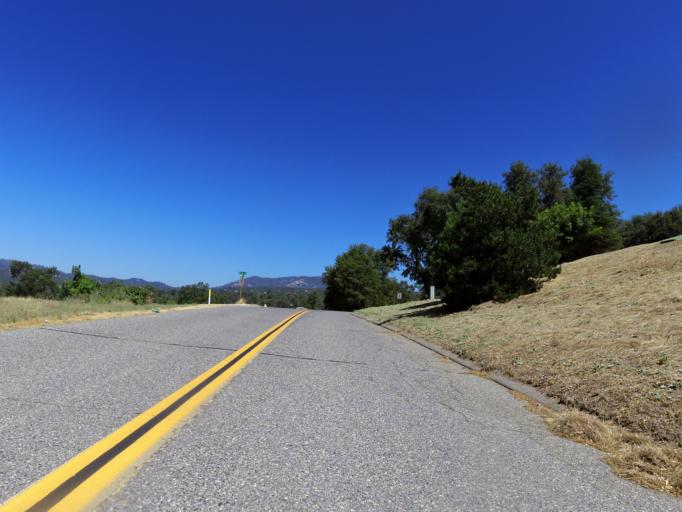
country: US
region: California
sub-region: Madera County
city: Ahwahnee
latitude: 37.3661
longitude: -119.6998
